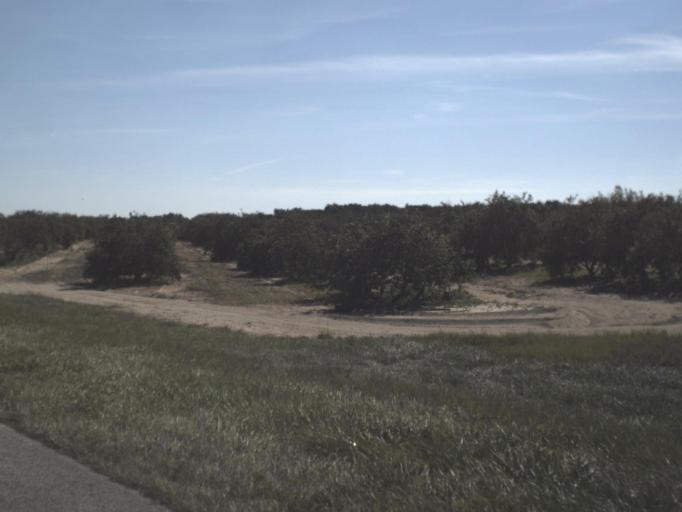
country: US
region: Florida
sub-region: Highlands County
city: Lake Placid
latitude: 27.2595
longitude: -81.3441
